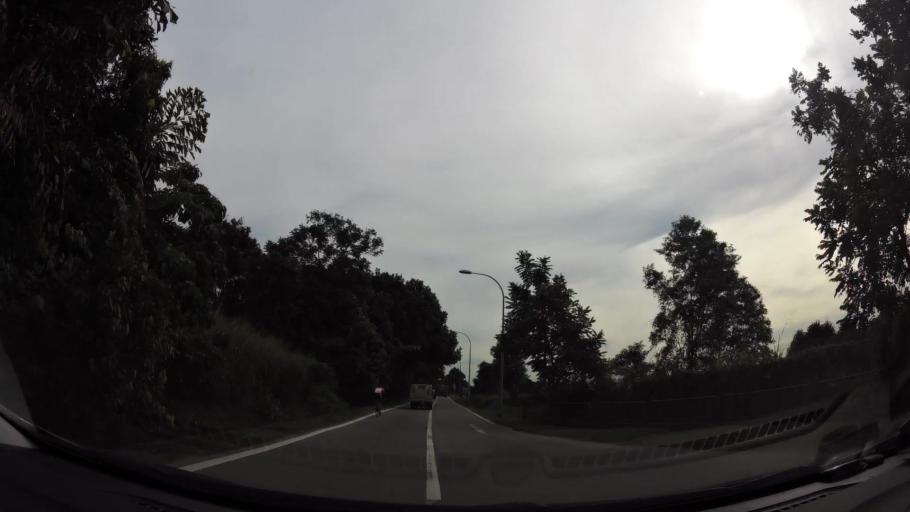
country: MY
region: Johor
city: Johor Bahru
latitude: 1.4337
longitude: 103.7250
